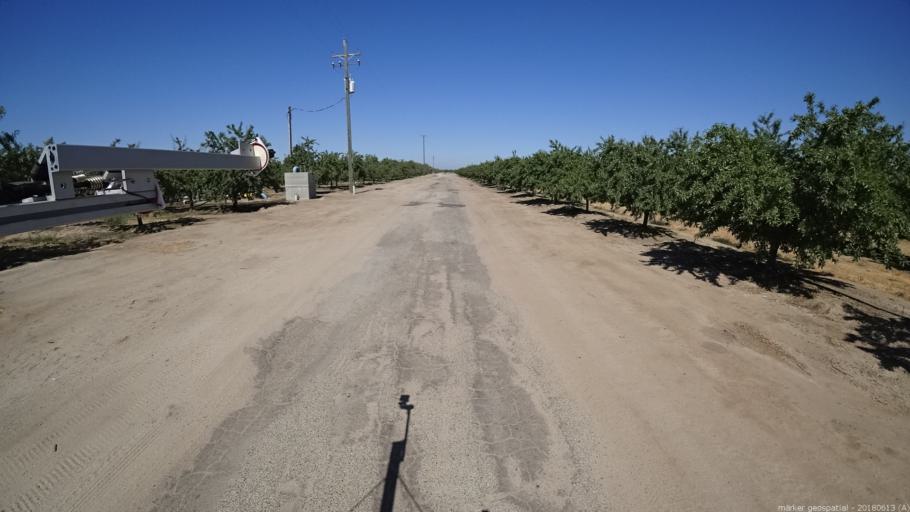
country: US
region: California
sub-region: Madera County
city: Chowchilla
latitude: 37.0762
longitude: -120.4440
